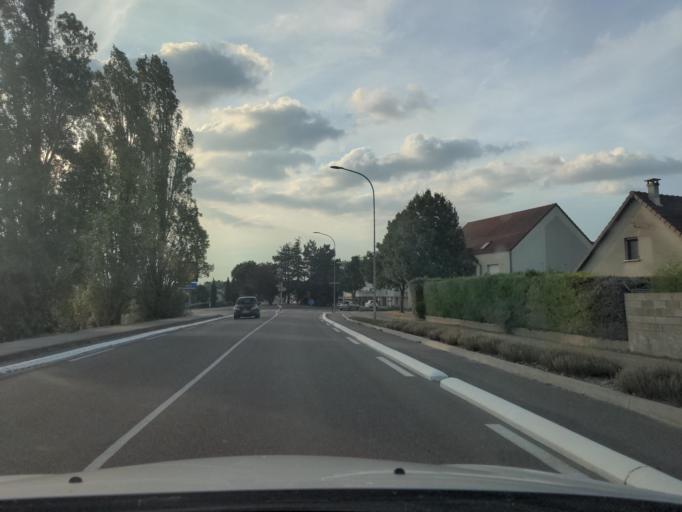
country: FR
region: Bourgogne
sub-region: Departement de la Cote-d'Or
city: Neuilly-les-Dijon
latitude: 47.2791
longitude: 5.1146
